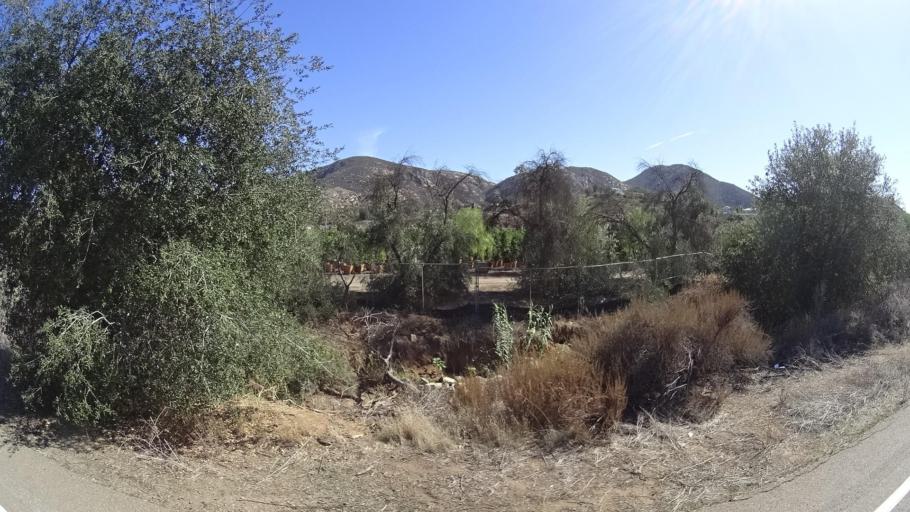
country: US
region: California
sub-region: San Diego County
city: Harbison Canyon
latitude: 32.8565
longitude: -116.8632
